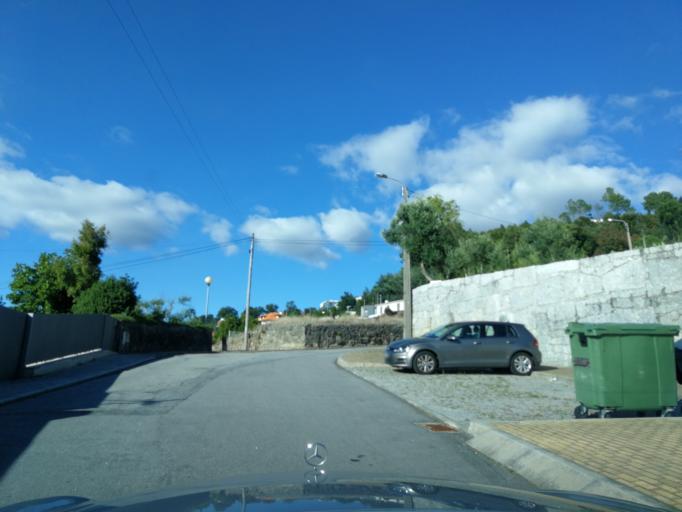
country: PT
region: Braga
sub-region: Braga
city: Adaufe
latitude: 41.5576
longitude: -8.3831
